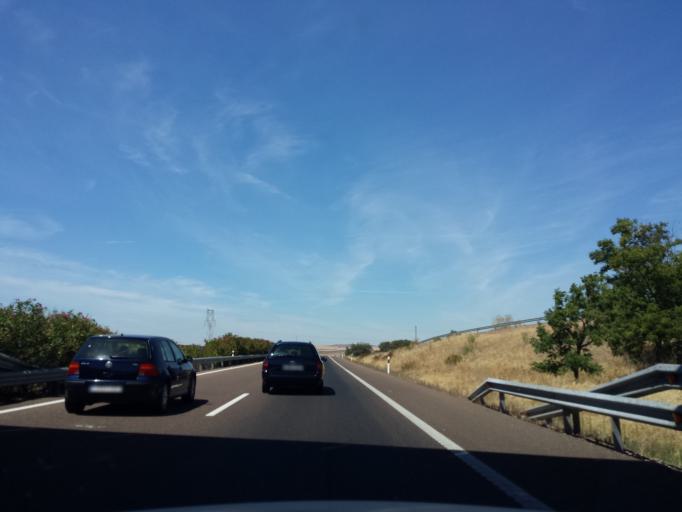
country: ES
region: Extremadura
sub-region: Provincia de Badajoz
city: San Pedro de Merida
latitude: 38.9504
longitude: -6.2196
